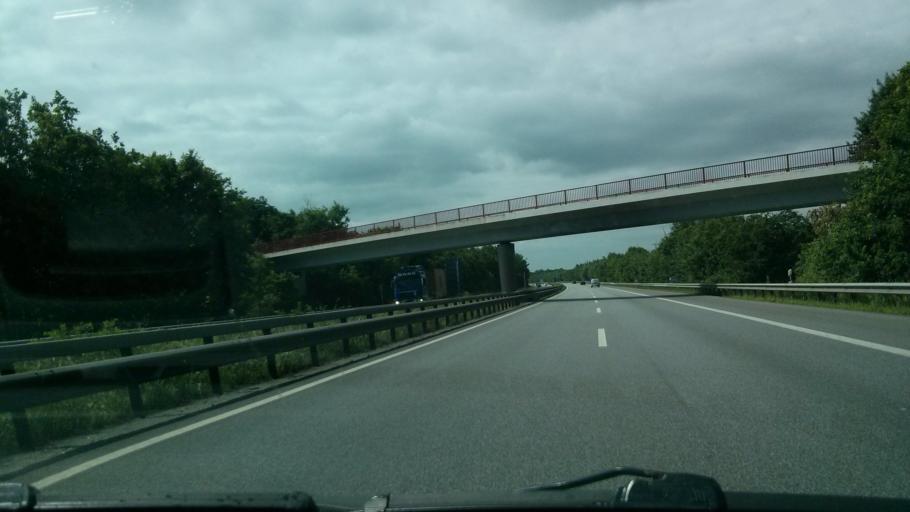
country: DE
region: Lower Saxony
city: Loxstedt
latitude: 53.4604
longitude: 8.5959
